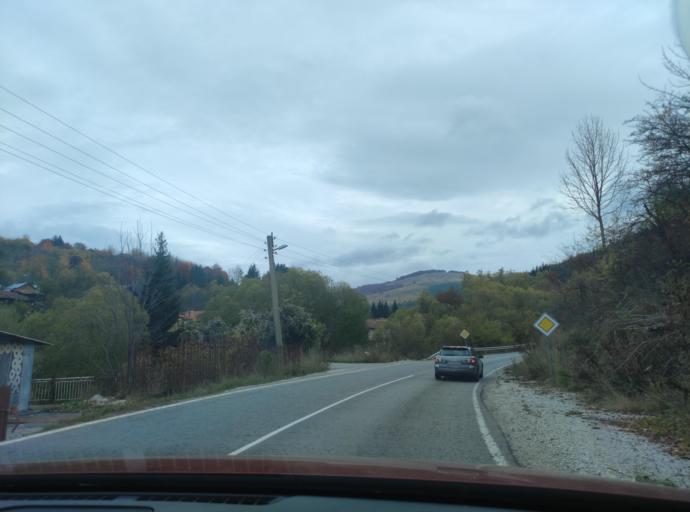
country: BG
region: Sofiya
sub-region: Obshtina Godech
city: Godech
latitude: 43.0696
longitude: 23.1078
